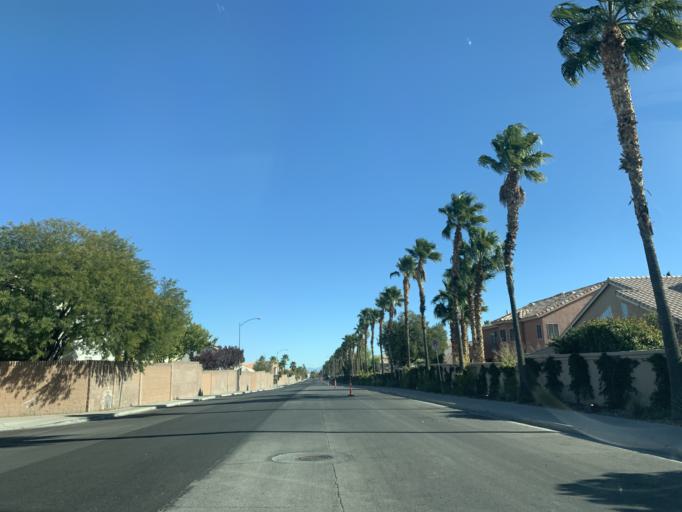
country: US
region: Nevada
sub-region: Clark County
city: Summerlin South
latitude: 36.1206
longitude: -115.3036
